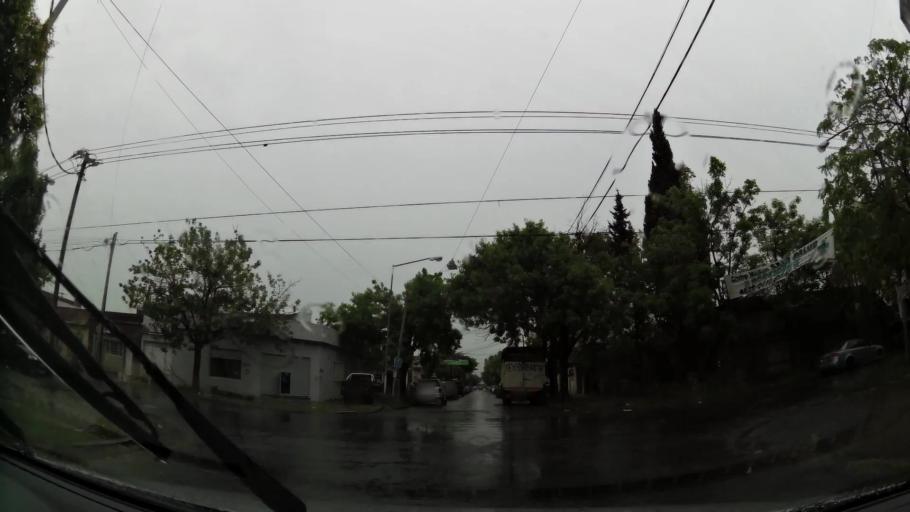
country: AR
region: Buenos Aires
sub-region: Partido de Lanus
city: Lanus
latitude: -34.7005
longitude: -58.4086
